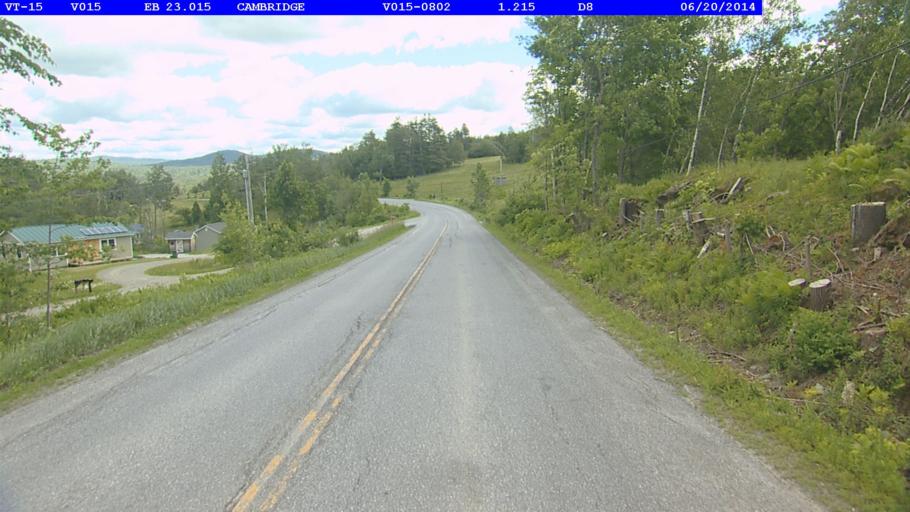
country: US
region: Vermont
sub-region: Chittenden County
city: Jericho
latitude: 44.6403
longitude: -72.8954
